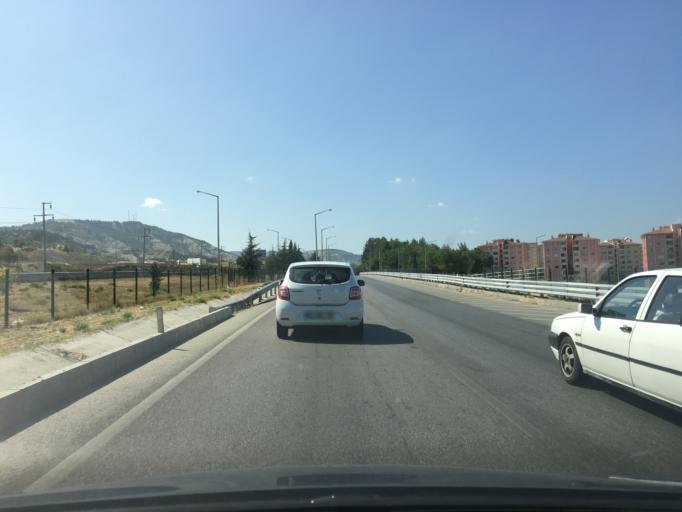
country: TR
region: Burdur
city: Burdur
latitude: 37.7379
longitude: 30.3116
